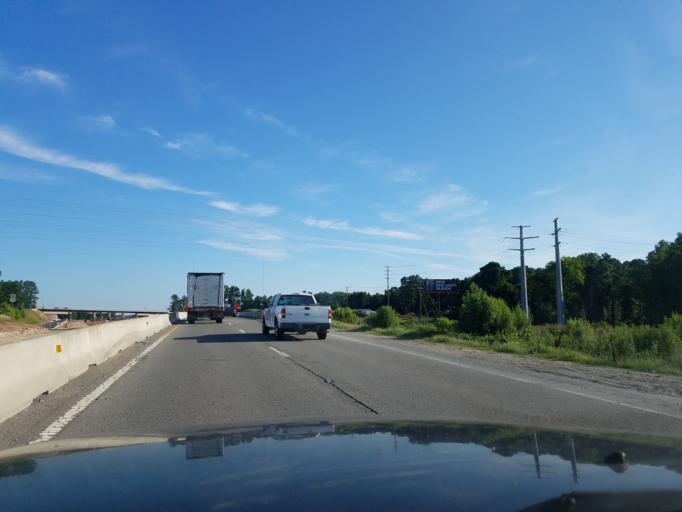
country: US
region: North Carolina
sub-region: Durham County
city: Durham
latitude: 35.9817
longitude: -78.8585
